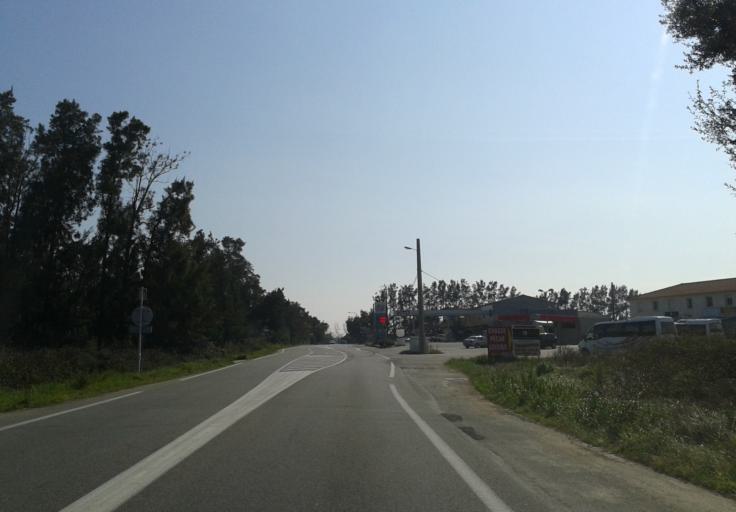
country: FR
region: Corsica
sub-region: Departement de la Haute-Corse
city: Linguizzetta
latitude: 42.2560
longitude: 9.5464
